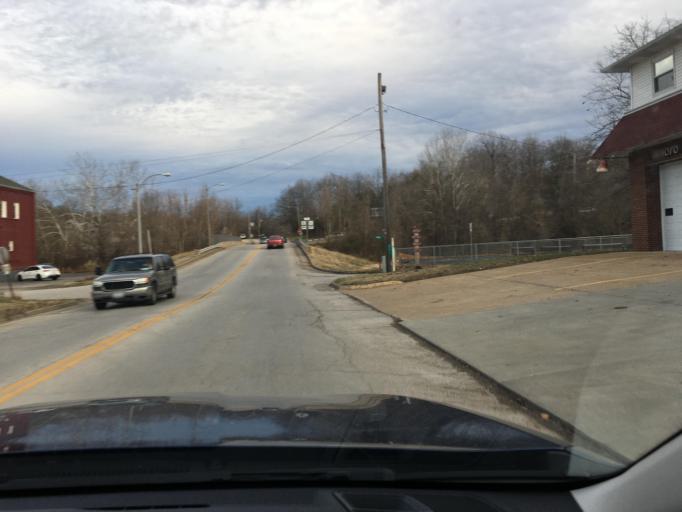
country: US
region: Missouri
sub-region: Jefferson County
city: De Soto
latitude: 38.1340
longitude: -90.5543
